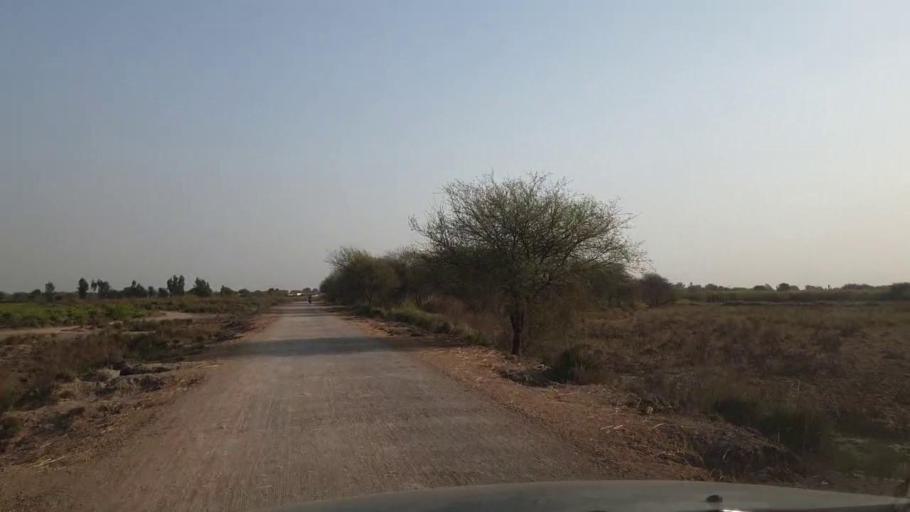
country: PK
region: Sindh
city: Bulri
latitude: 24.9488
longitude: 68.3421
